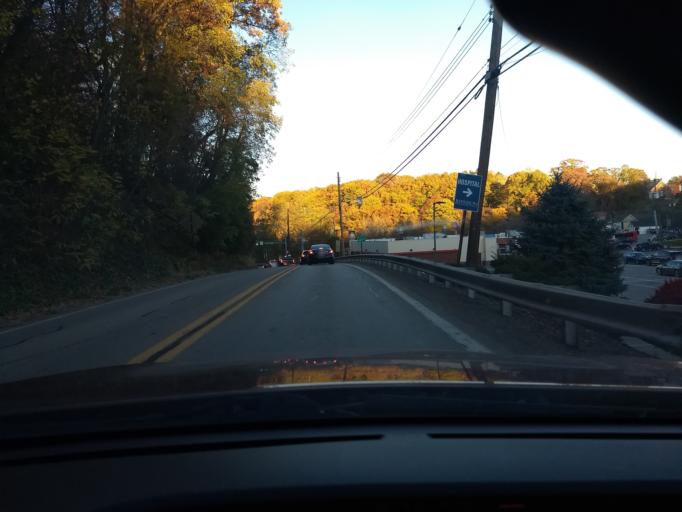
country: US
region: Pennsylvania
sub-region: Allegheny County
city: Baldwin
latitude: 40.3458
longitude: -79.9747
